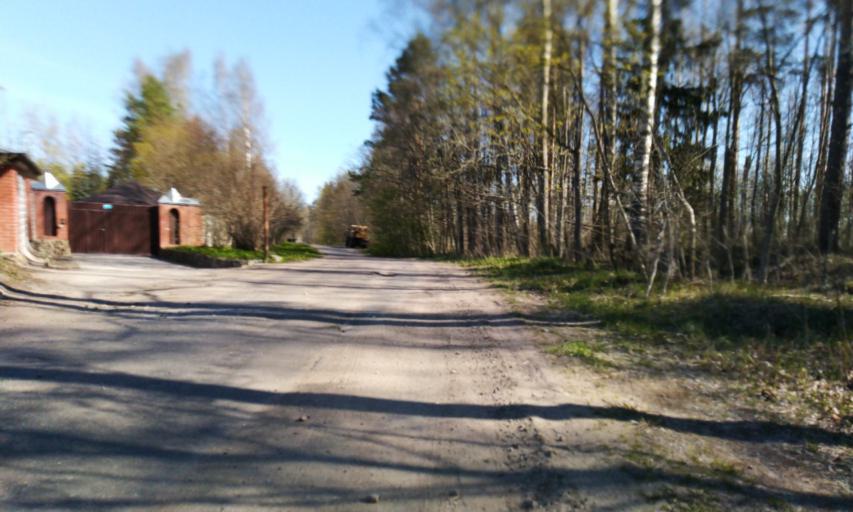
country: RU
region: Leningrad
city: Garbolovo
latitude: 60.3897
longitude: 30.4871
